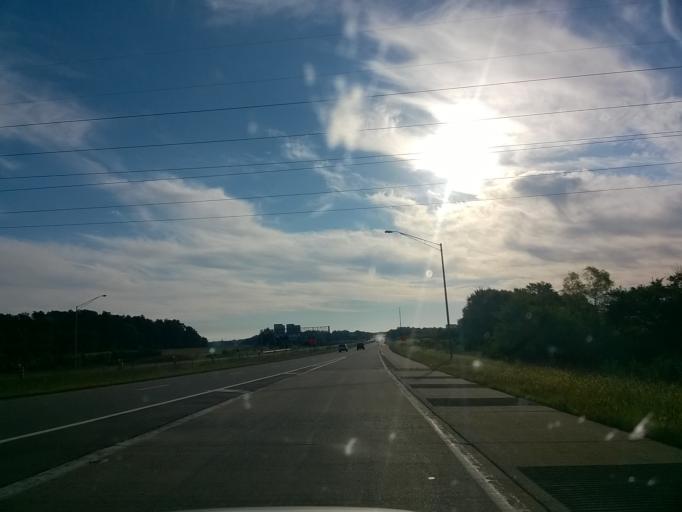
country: US
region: Indiana
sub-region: Gibson County
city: Haubstadt
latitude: 38.1695
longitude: -87.4641
